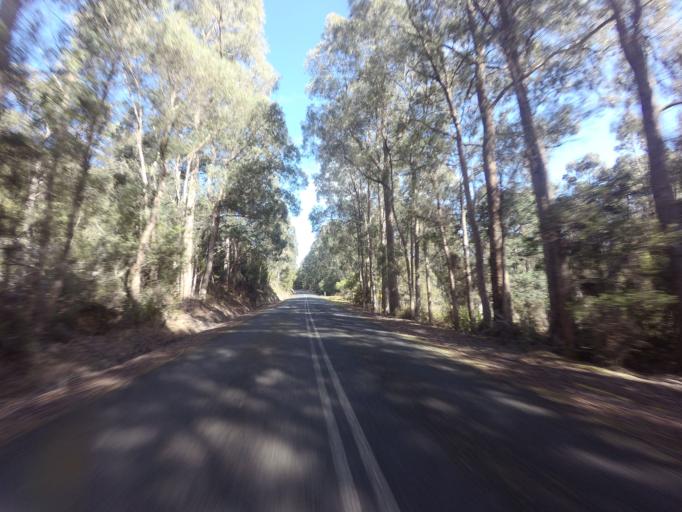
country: AU
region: Tasmania
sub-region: Derwent Valley
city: New Norfolk
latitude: -42.7688
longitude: 146.5765
